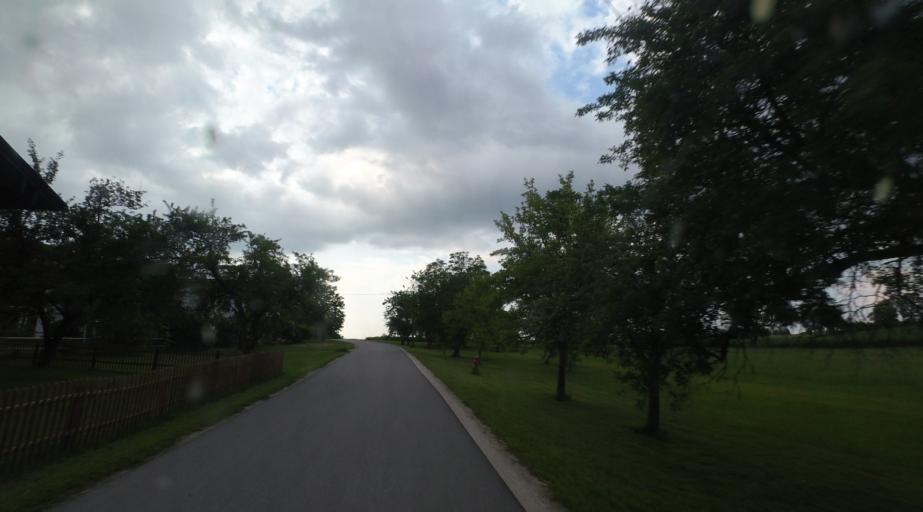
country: DE
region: Bavaria
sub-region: Upper Bavaria
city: Grabenstatt
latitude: 47.8338
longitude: 12.5458
